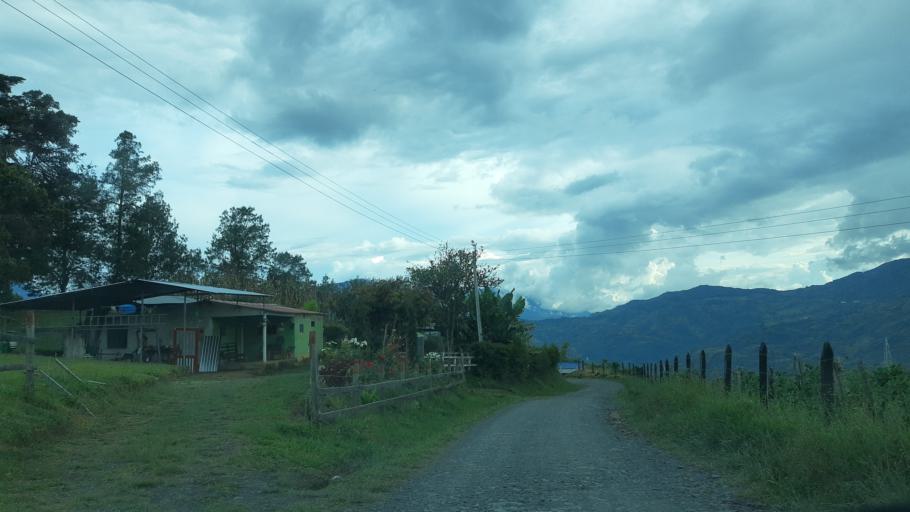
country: CO
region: Boyaca
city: Garagoa
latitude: 4.9868
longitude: -73.3307
